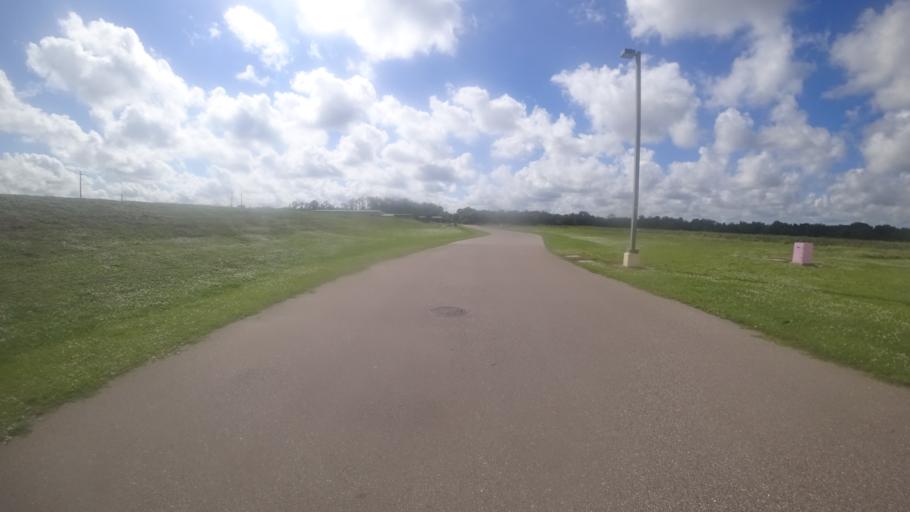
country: US
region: Florida
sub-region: Manatee County
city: Samoset
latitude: 27.4665
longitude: -82.4474
